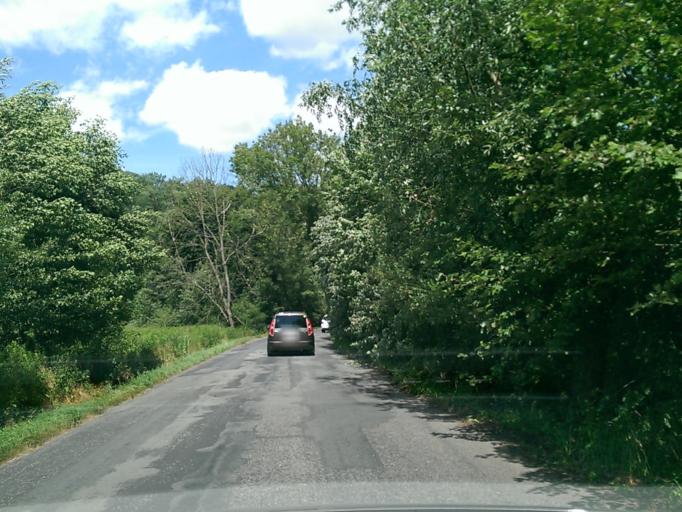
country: CZ
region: Central Bohemia
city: Mseno
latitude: 50.3987
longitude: 14.5581
